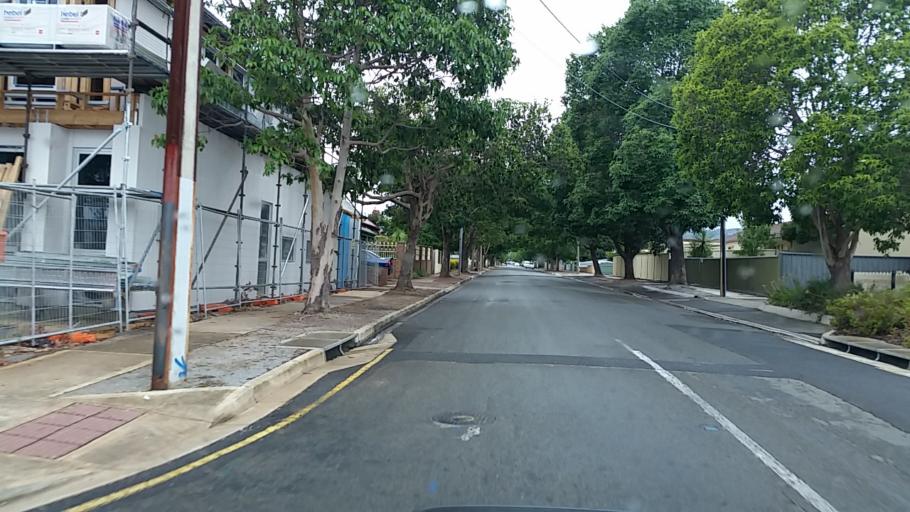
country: AU
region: South Australia
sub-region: Campbelltown
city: Hectorville
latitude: -34.9002
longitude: 138.6516
